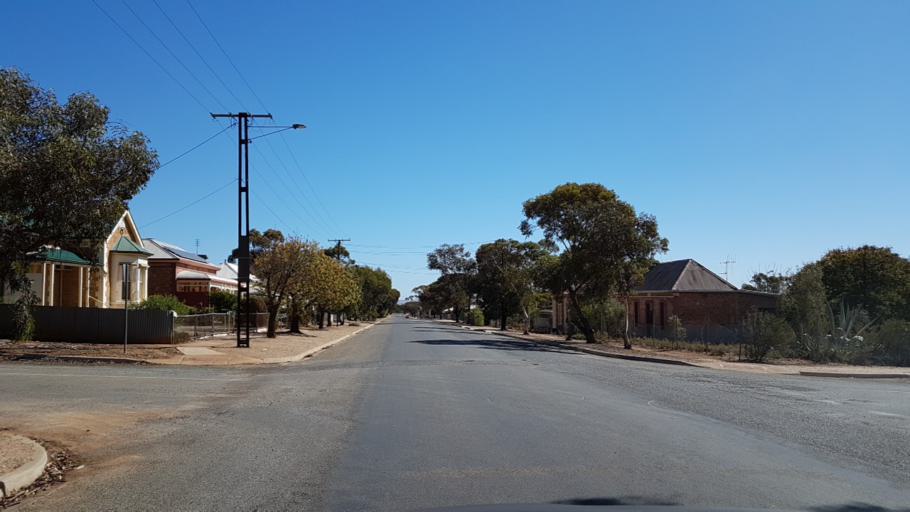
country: AU
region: South Australia
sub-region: Peterborough
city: Peterborough
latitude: -32.9787
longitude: 138.8294
